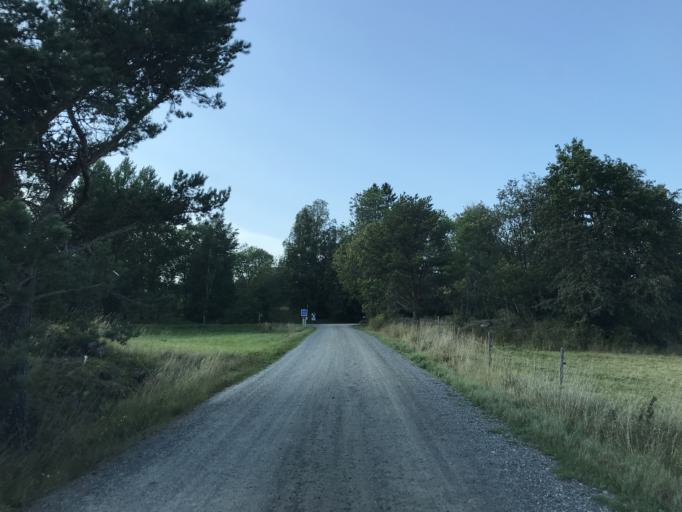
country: SE
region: Stockholm
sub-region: Norrtalje Kommun
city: Bjorko
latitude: 59.8503
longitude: 19.0129
